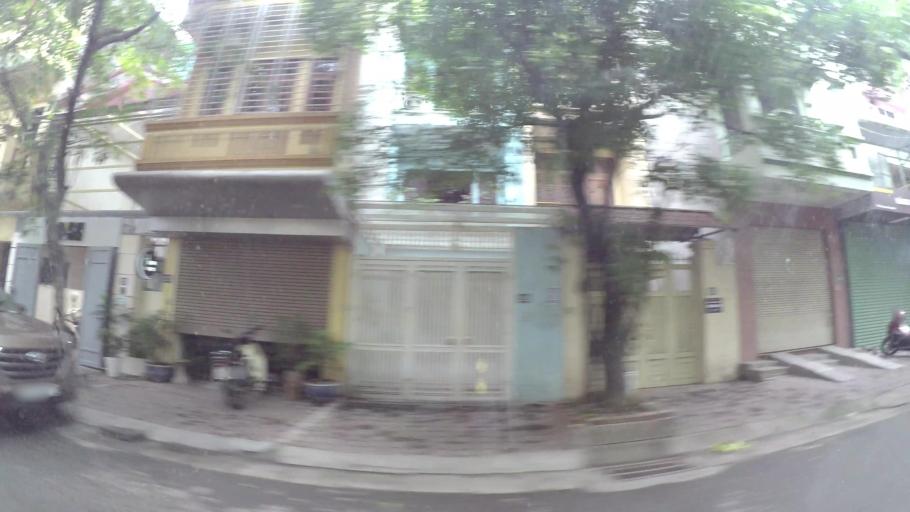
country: VN
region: Ha Noi
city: Dong Da
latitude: 21.0180
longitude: 105.8250
